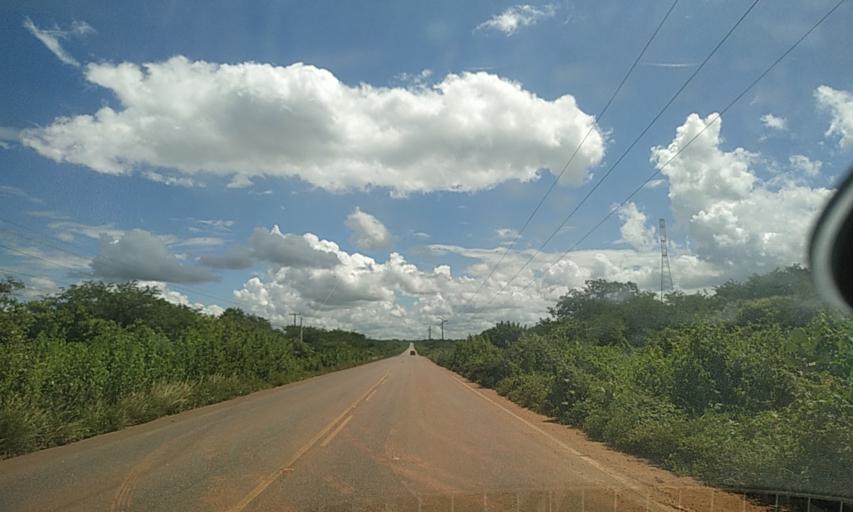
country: BR
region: Rio Grande do Norte
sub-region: Mossoro
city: Mossoro
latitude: -5.1630
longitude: -37.4274
